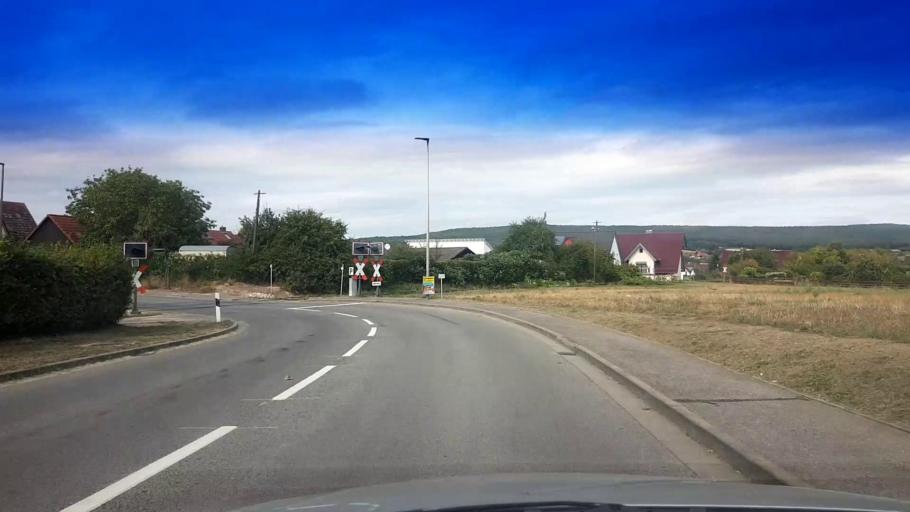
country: DE
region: Bavaria
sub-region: Upper Franconia
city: Frensdorf
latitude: 49.8151
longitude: 10.8715
